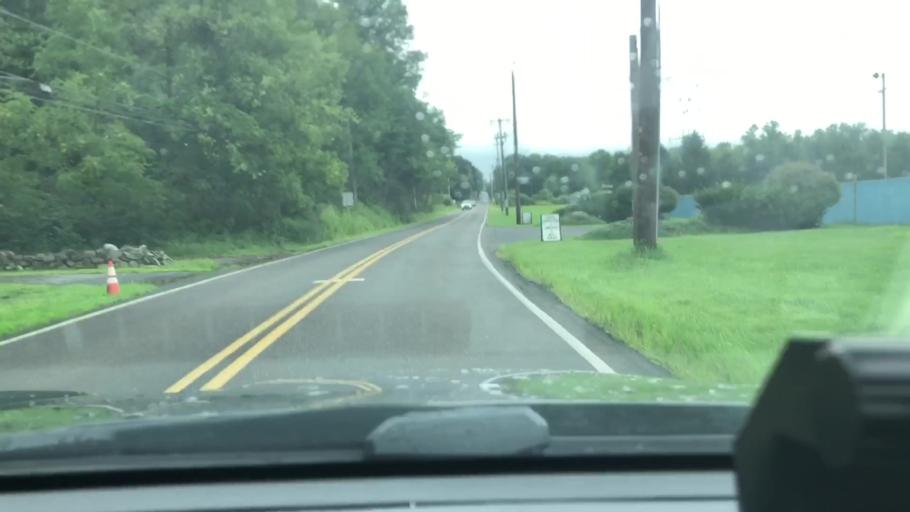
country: US
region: Pennsylvania
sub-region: Lehigh County
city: Coopersburg
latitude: 40.4908
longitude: -75.3955
